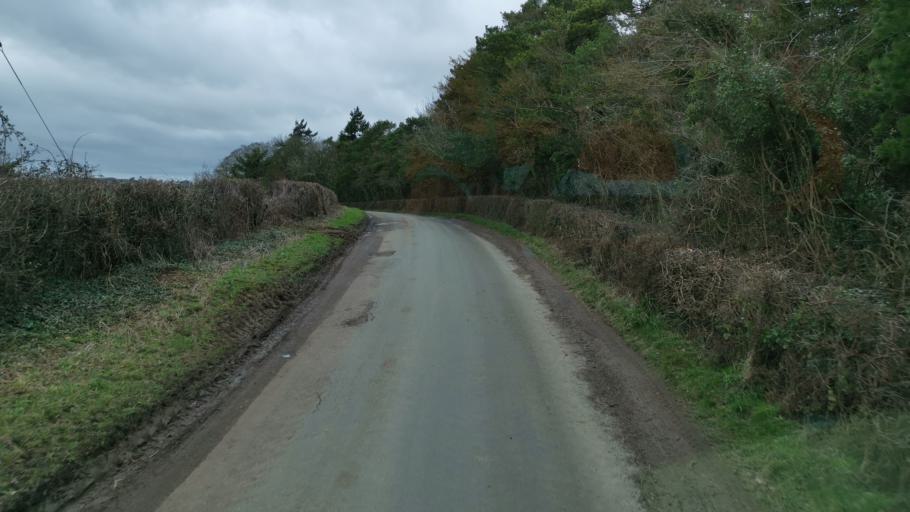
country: GB
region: England
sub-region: Oxfordshire
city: Somerton
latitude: 51.8998
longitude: -1.3091
